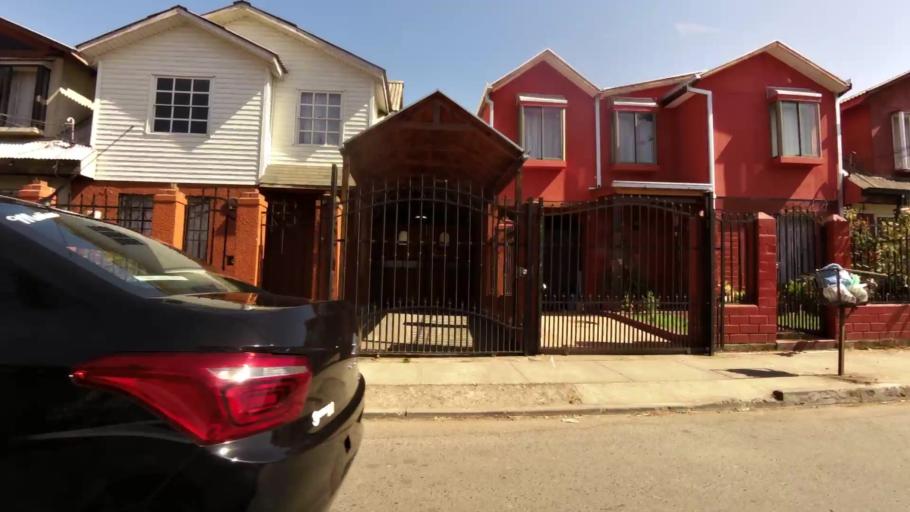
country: CL
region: Maule
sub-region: Provincia de Talca
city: Talca
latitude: -35.4093
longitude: -71.6371
